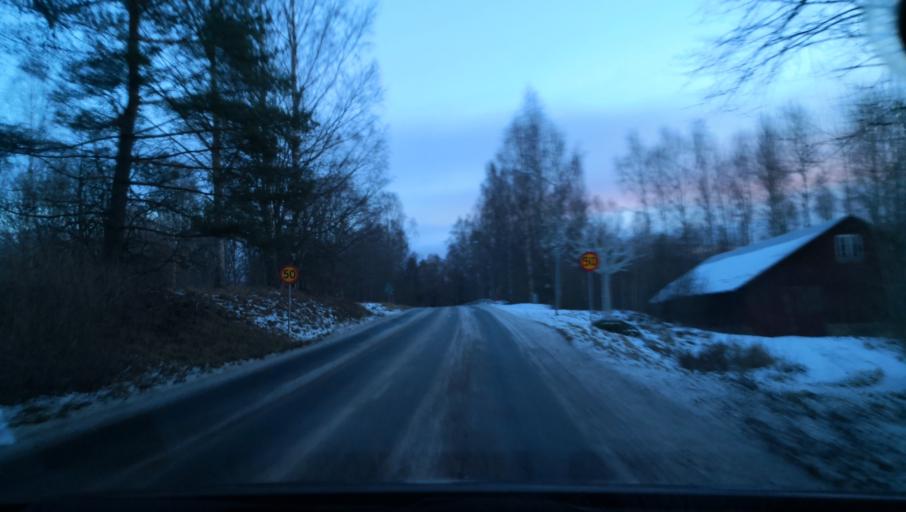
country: SE
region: Soedermanland
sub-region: Katrineholms Kommun
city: Katrineholm
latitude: 59.0877
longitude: 16.2154
